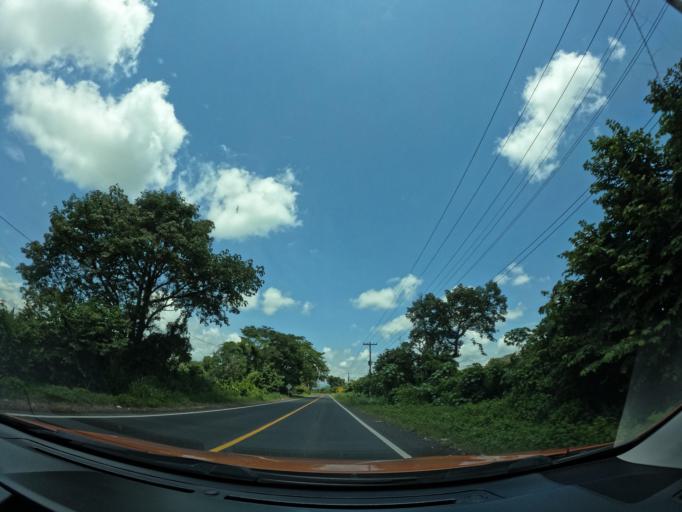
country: GT
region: Escuintla
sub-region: Municipio de Masagua
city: Masagua
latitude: 14.1550
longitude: -90.8814
